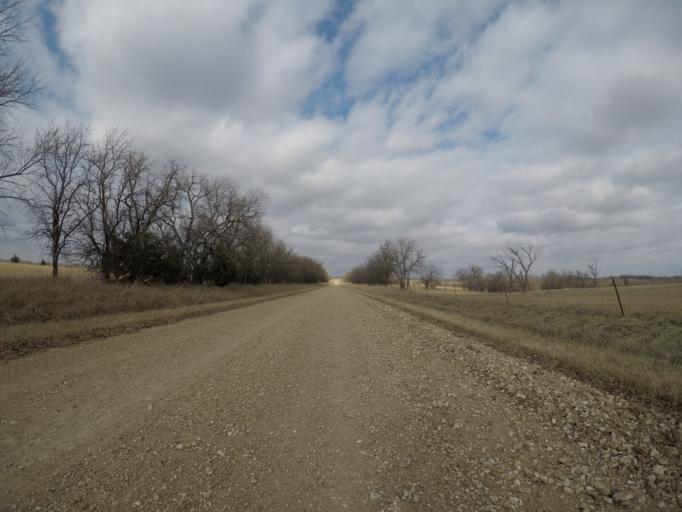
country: US
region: Kansas
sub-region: Morris County
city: Council Grove
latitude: 38.7843
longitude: -96.3527
